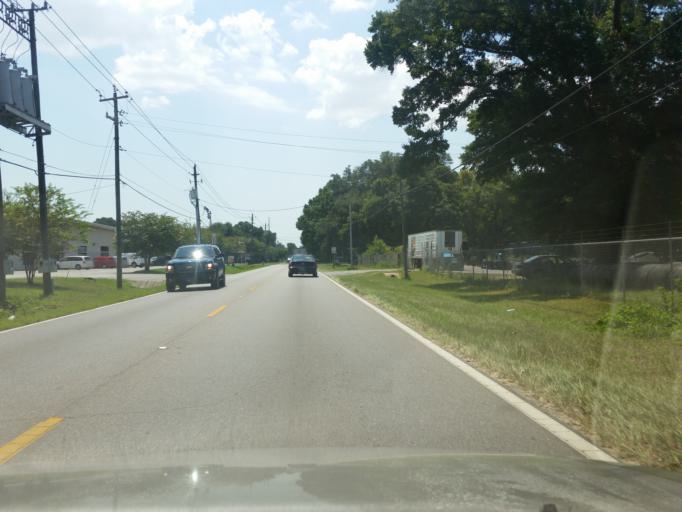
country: US
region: Florida
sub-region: Escambia County
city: Ensley
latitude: 30.5419
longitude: -87.2783
